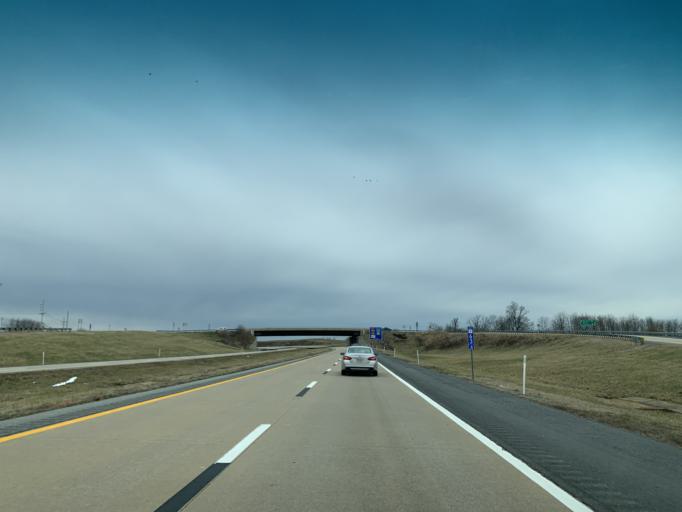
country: US
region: West Virginia
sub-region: Jefferson County
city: Ranson
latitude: 39.3352
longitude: -77.8561
